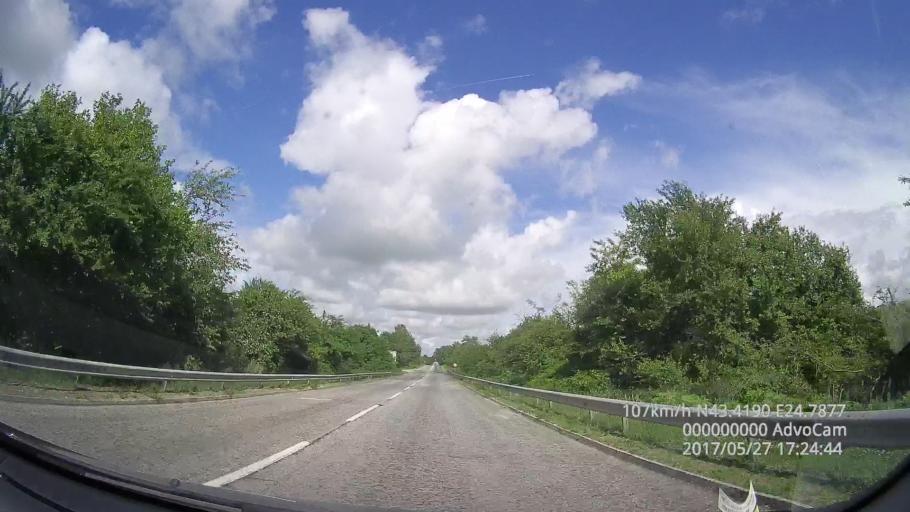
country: BG
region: Pleven
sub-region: Obshtina Pordim
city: Pordim
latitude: 43.4191
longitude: 24.7888
